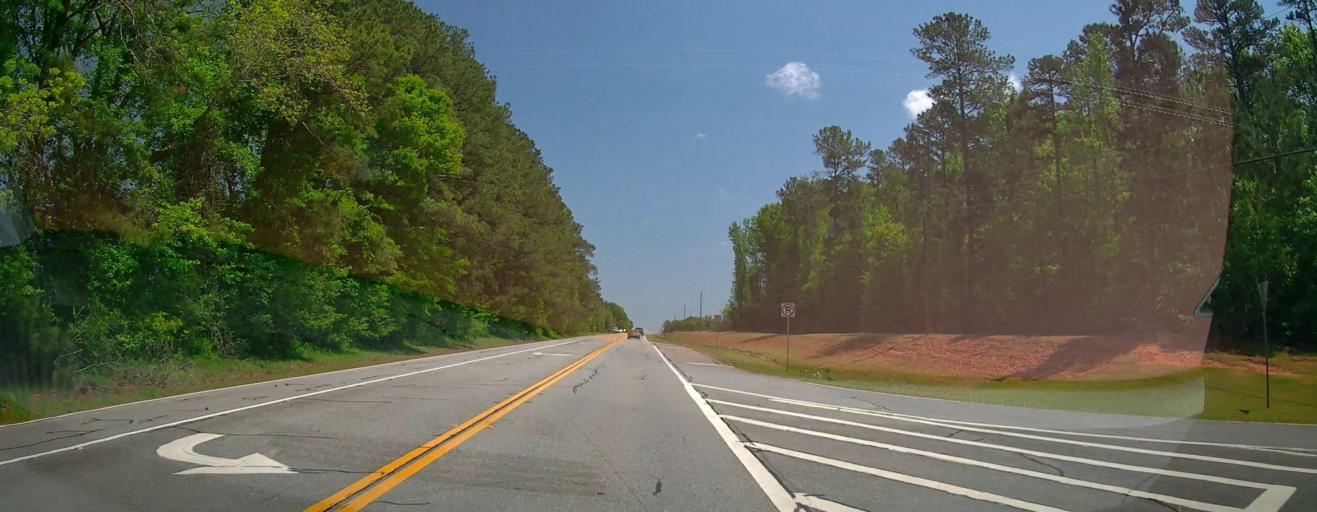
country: US
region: Georgia
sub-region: Jasper County
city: Monticello
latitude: 33.3109
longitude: -83.7055
